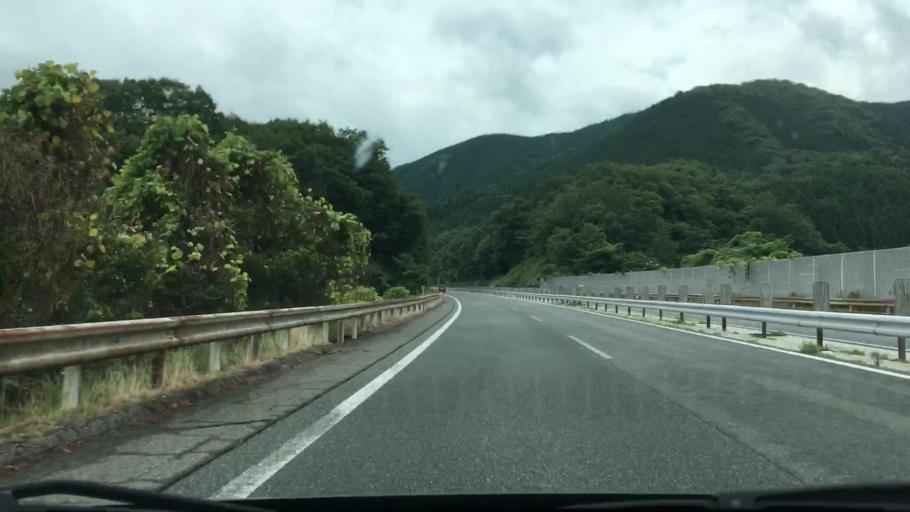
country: JP
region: Okayama
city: Niimi
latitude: 34.9612
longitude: 133.3324
